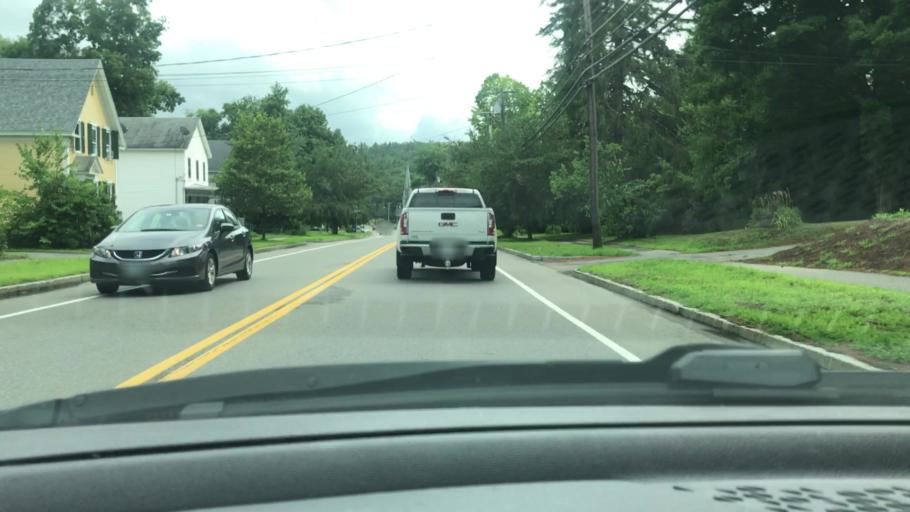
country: US
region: New Hampshire
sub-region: Merrimack County
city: East Concord
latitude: 43.2480
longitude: -71.5716
